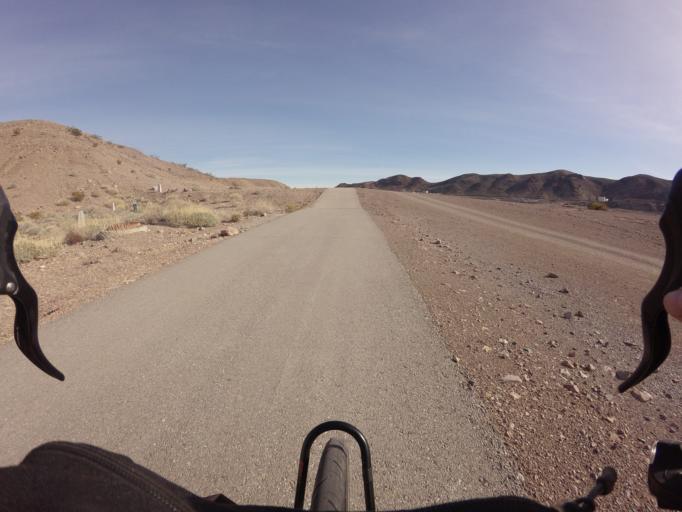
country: US
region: Nevada
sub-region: Clark County
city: Boulder City
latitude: 36.0646
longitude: -114.8134
